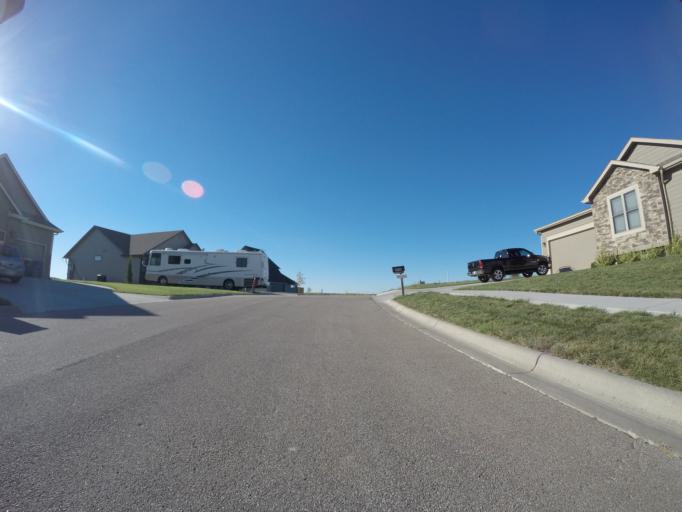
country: US
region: Kansas
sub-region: Riley County
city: Manhattan
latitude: 39.2092
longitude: -96.6293
